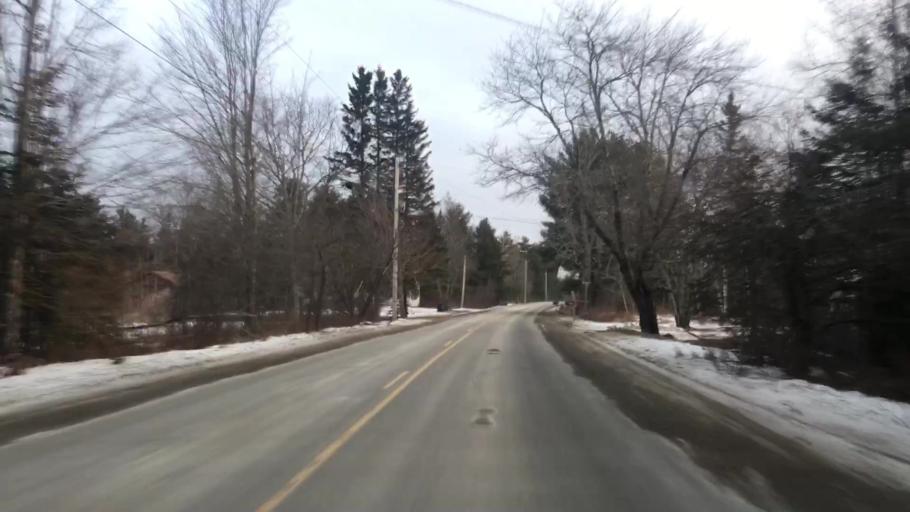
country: US
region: Maine
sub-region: Hancock County
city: Franklin
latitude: 44.6891
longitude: -68.3490
